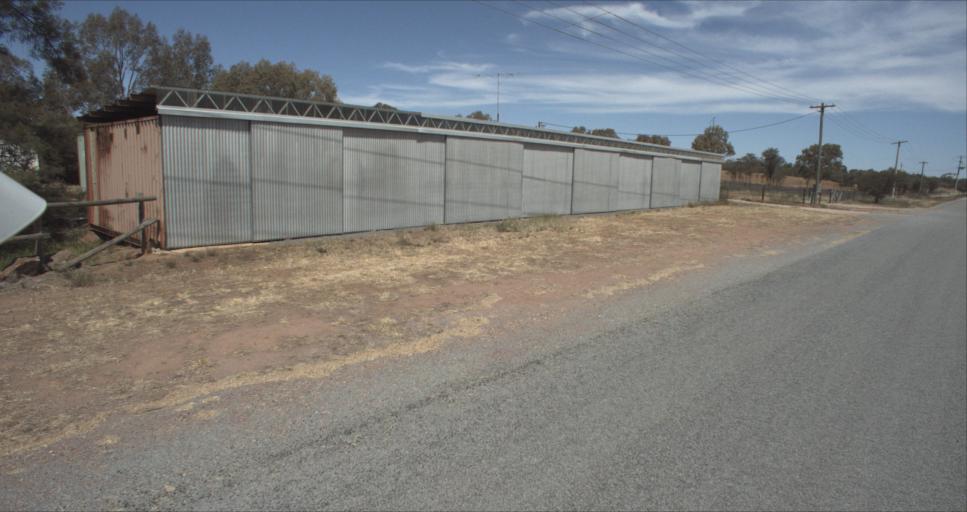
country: AU
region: New South Wales
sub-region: Leeton
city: Leeton
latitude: -34.5783
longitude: 146.4326
